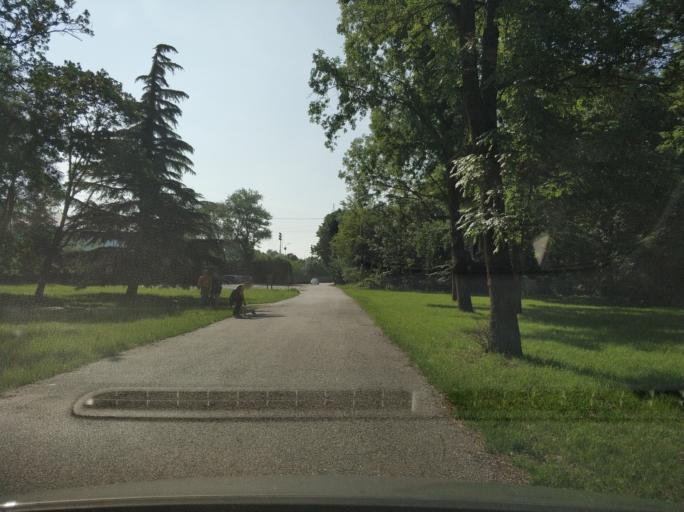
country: IT
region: Piedmont
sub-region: Provincia di Torino
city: Cafasse
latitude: 45.2479
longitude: 7.5267
